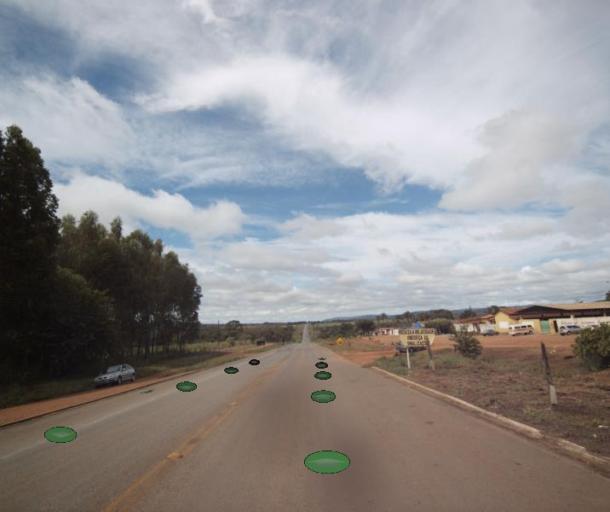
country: BR
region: Goias
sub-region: Barro Alto
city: Barro Alto
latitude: -15.2097
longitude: -48.6996
